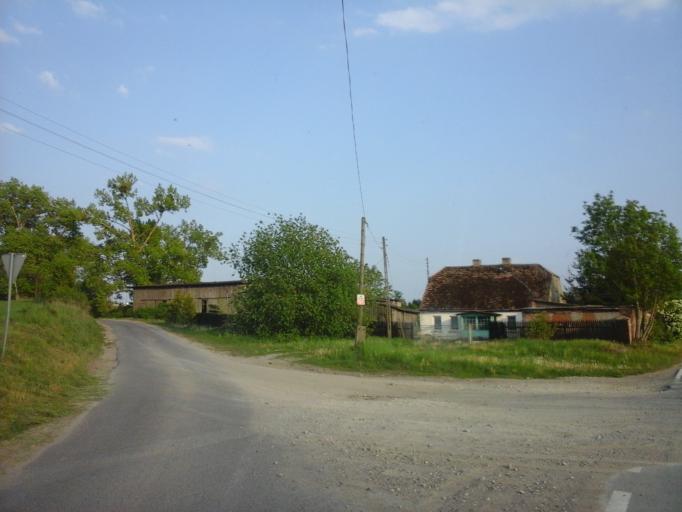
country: PL
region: West Pomeranian Voivodeship
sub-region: Powiat choszczenski
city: Krzecin
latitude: 52.9987
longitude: 15.4252
